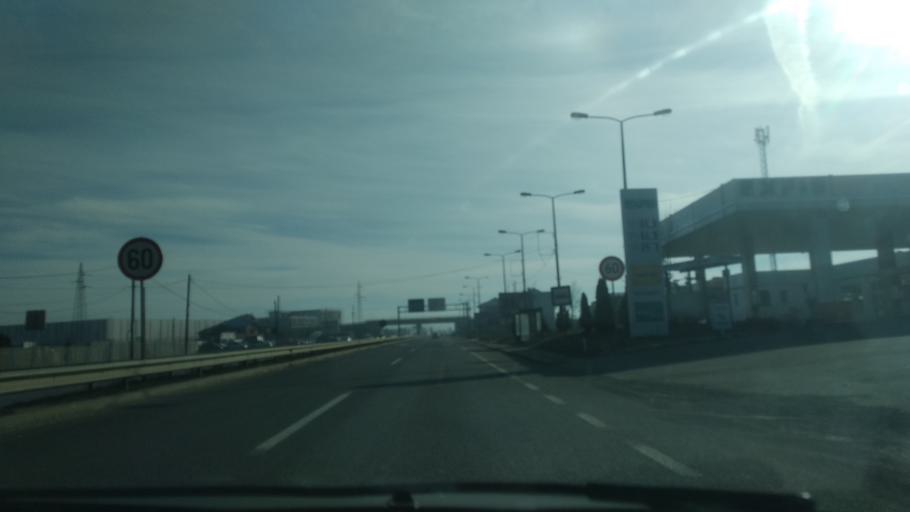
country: XK
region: Pristina
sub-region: Komuna e Obiliqit
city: Obiliq
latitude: 42.7191
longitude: 21.0904
